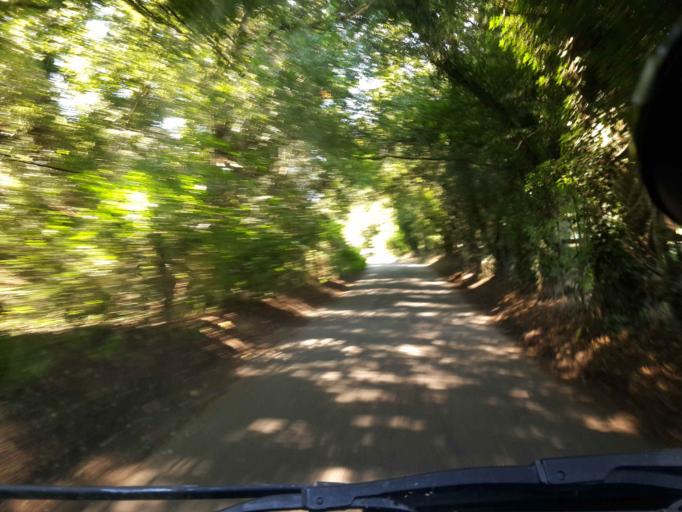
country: GB
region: England
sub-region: Surrey
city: Chilworth
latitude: 51.2078
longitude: -0.4777
